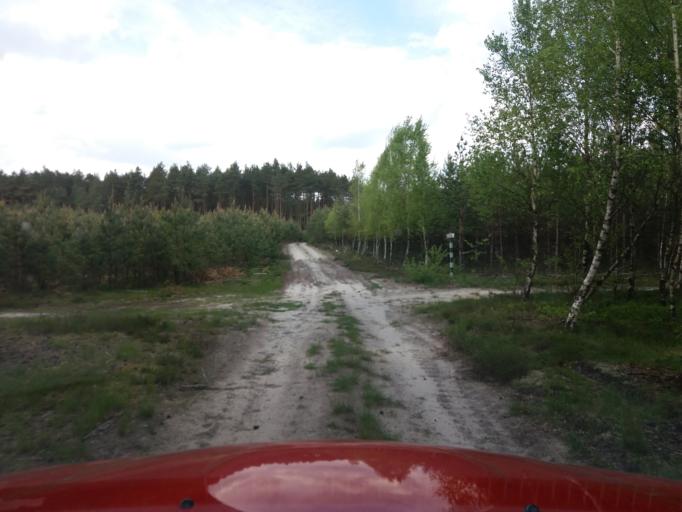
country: PL
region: West Pomeranian Voivodeship
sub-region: Powiat choszczenski
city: Drawno
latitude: 53.1208
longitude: 15.7601
